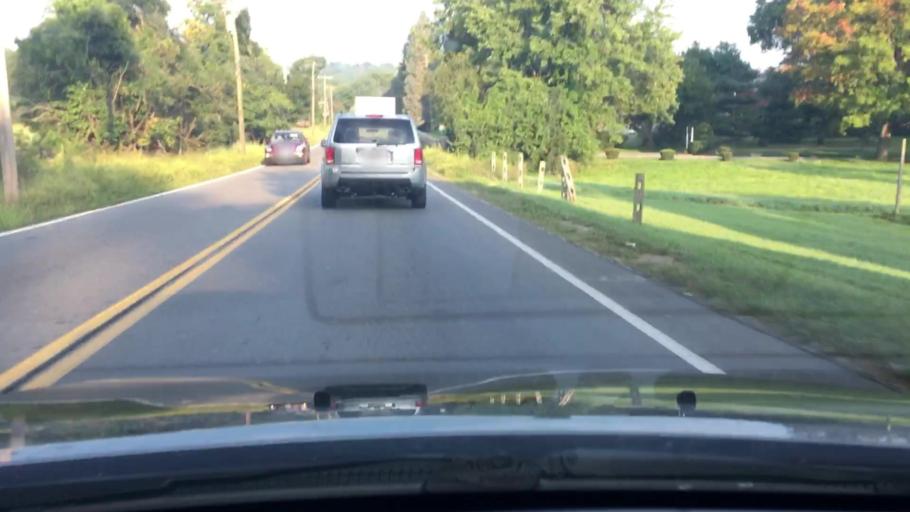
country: US
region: Massachusetts
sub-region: Worcester County
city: Westborough
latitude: 42.2577
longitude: -71.5993
